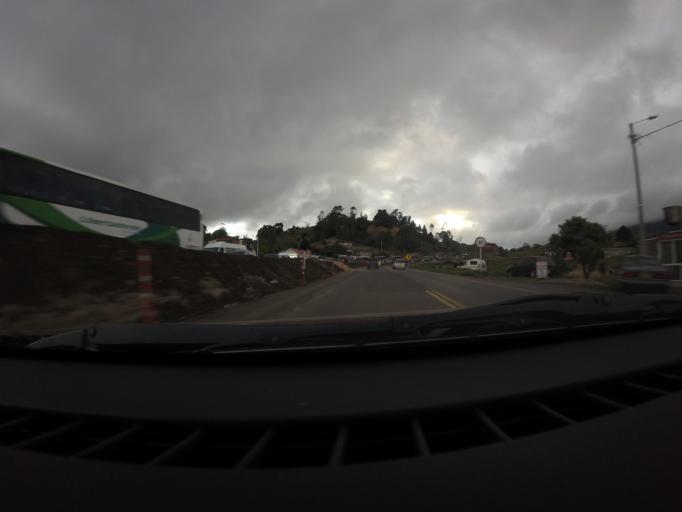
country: CO
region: Boyaca
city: Samaca
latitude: 5.4414
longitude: -73.4383
